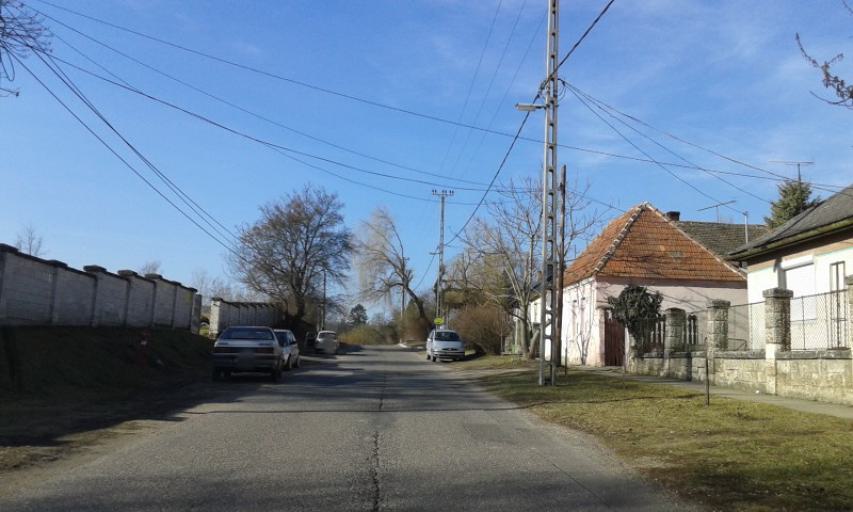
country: HU
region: Pest
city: Soskut
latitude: 47.4030
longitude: 18.8249
